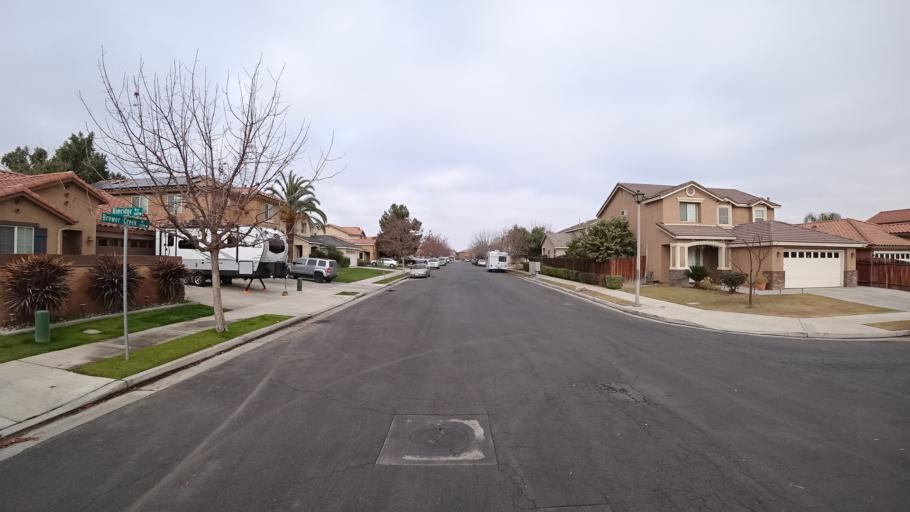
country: US
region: California
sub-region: Kern County
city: Greenfield
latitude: 35.2980
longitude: -119.0766
